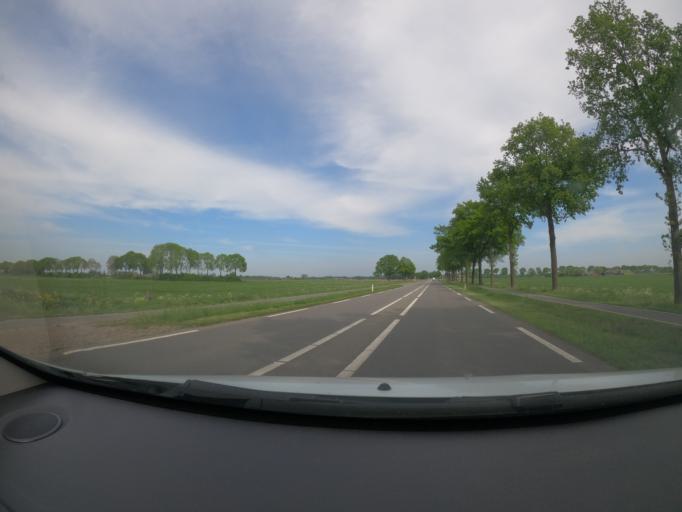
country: NL
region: Gelderland
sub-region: Gemeente Montferland
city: s-Heerenberg
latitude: 51.8976
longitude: 6.2914
